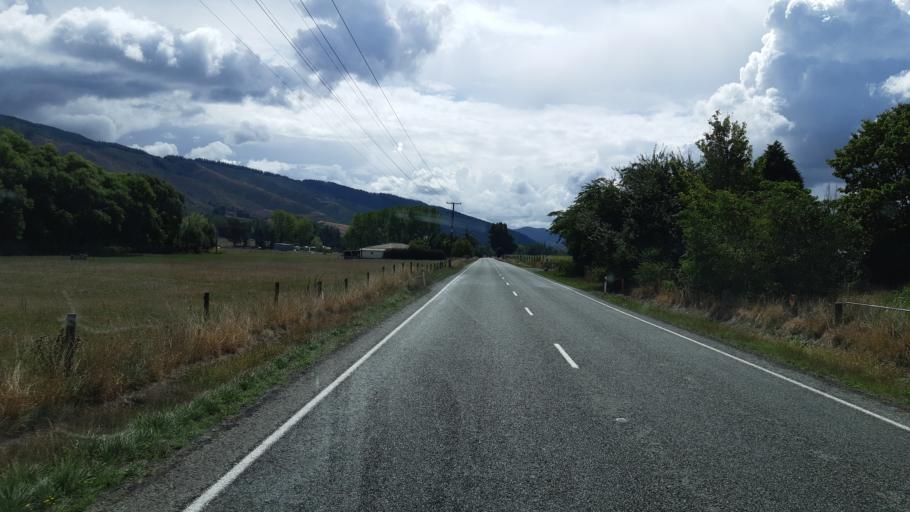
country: NZ
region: Tasman
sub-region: Tasman District
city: Wakefield
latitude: -41.4706
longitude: 172.8067
